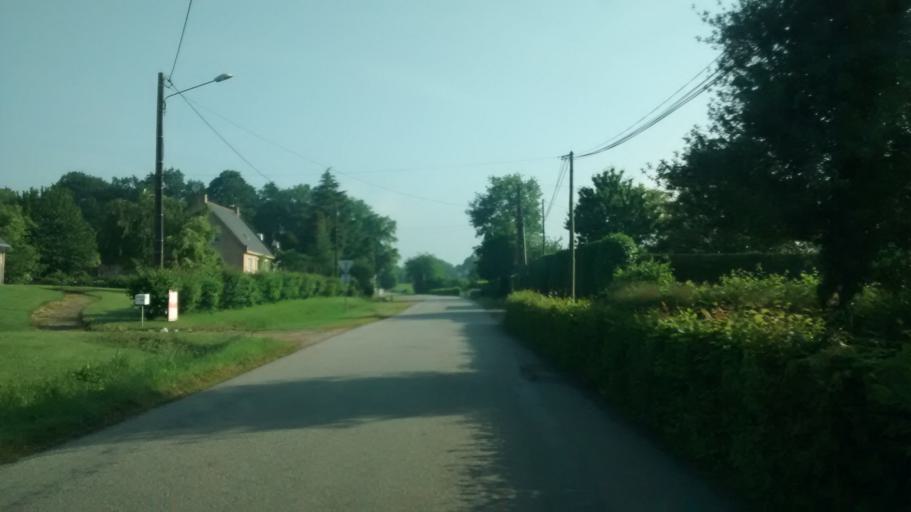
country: FR
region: Brittany
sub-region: Departement du Morbihan
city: Ruffiac
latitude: 47.8206
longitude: -2.2828
